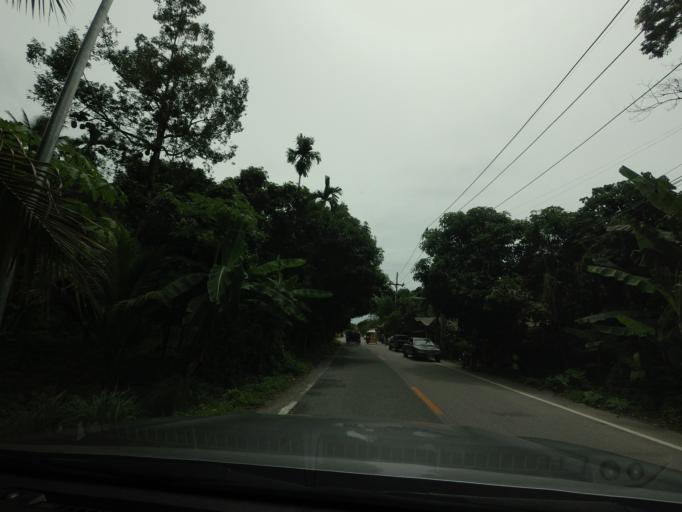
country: TH
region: Pattani
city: Sai Buri
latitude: 6.6491
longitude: 101.5536
